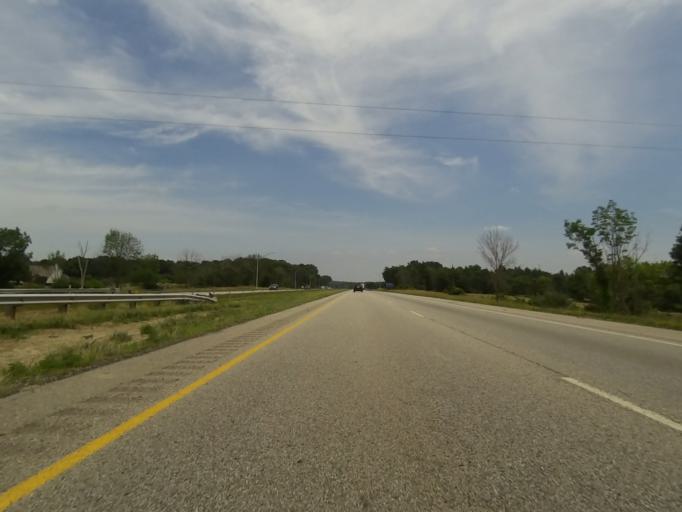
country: US
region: Ohio
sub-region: Portage County
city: Ravenna
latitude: 41.1056
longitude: -81.1218
